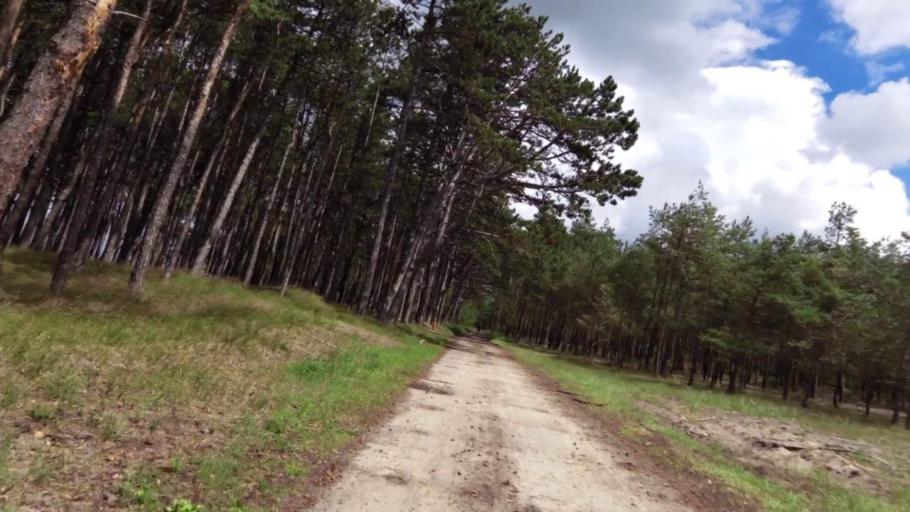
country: PL
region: West Pomeranian Voivodeship
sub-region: Powiat slawienski
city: Darlowo
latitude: 54.4986
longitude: 16.4521
